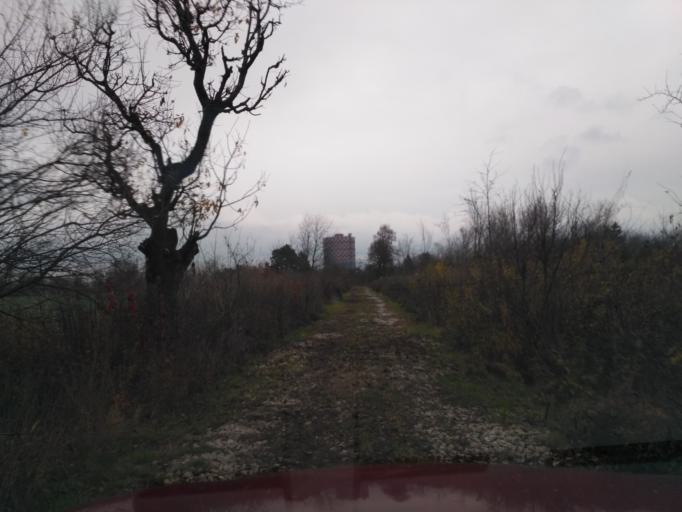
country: SK
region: Kosicky
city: Kosice
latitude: 48.6026
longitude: 21.1642
